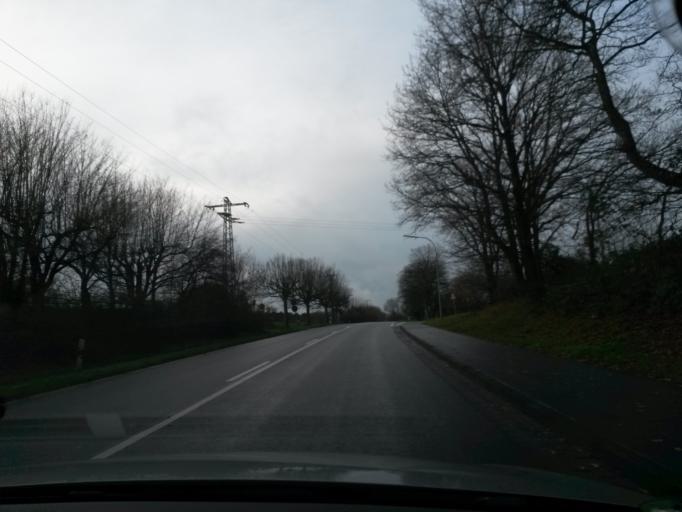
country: DE
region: North Rhine-Westphalia
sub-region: Regierungsbezirk Dusseldorf
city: Alpen
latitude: 51.5709
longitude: 6.5033
